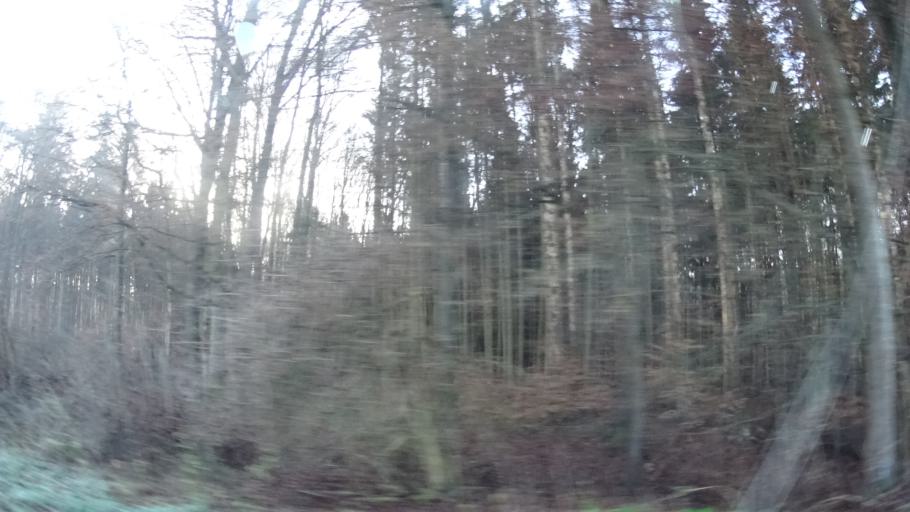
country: DE
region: Bavaria
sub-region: Regierungsbezirk Unterfranken
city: Neunkirchen
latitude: 49.7305
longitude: 9.3913
